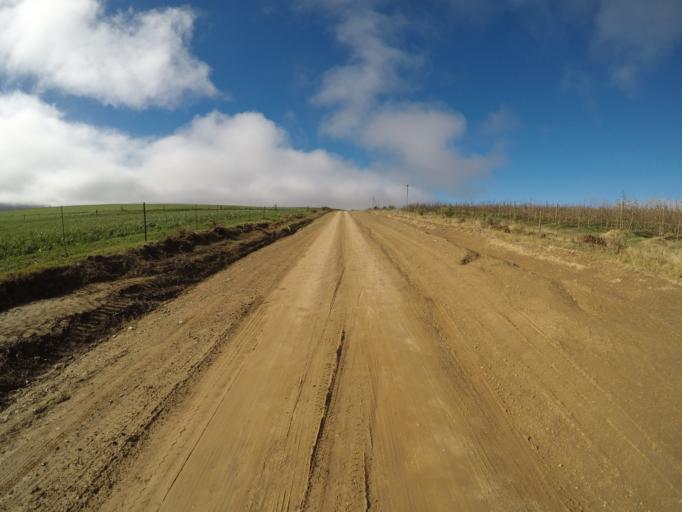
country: ZA
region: Western Cape
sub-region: Overberg District Municipality
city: Caledon
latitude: -34.1093
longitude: 19.7584
